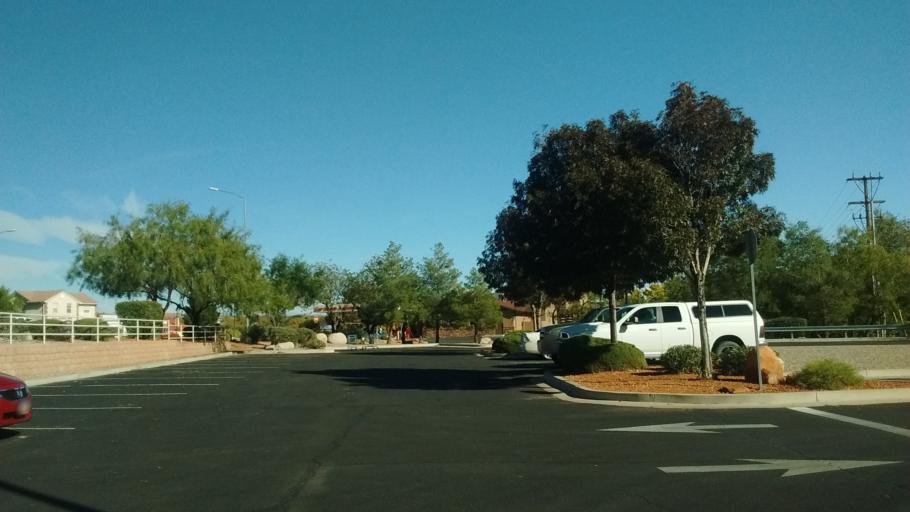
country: US
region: Utah
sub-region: Washington County
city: Washington
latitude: 37.1286
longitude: -113.5190
